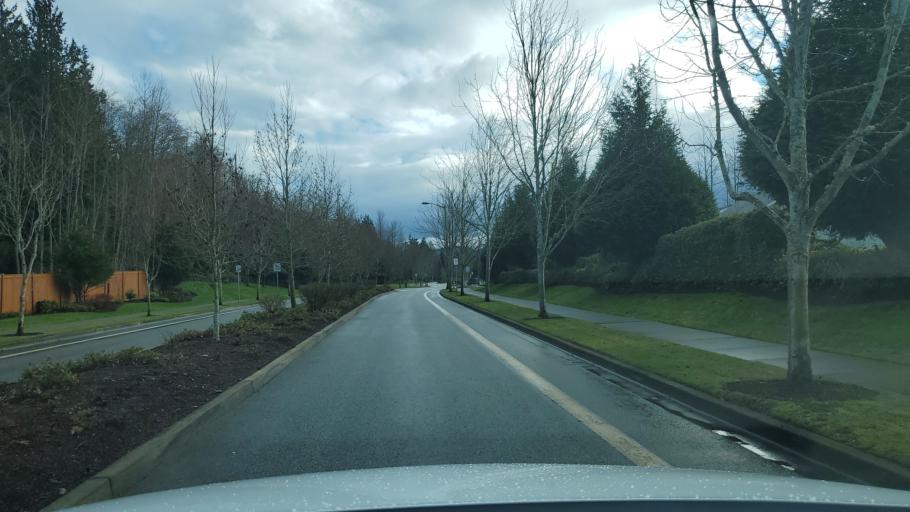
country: US
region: Washington
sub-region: Skagit County
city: Big Lake
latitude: 48.4250
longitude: -122.2784
